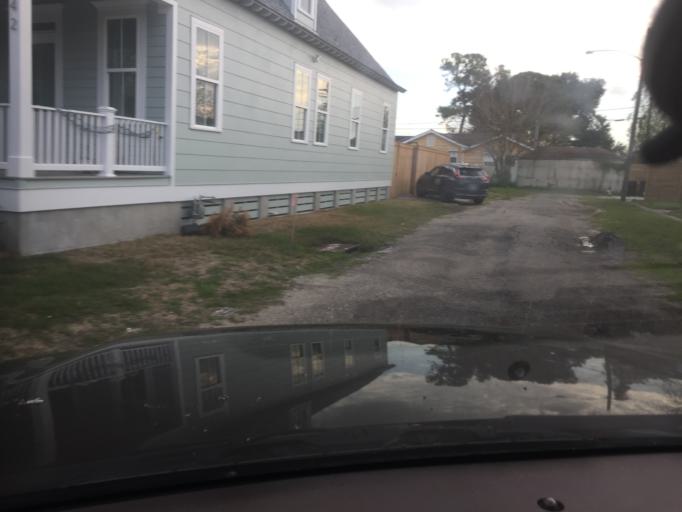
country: US
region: Louisiana
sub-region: Orleans Parish
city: New Orleans
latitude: 29.9877
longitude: -90.0818
